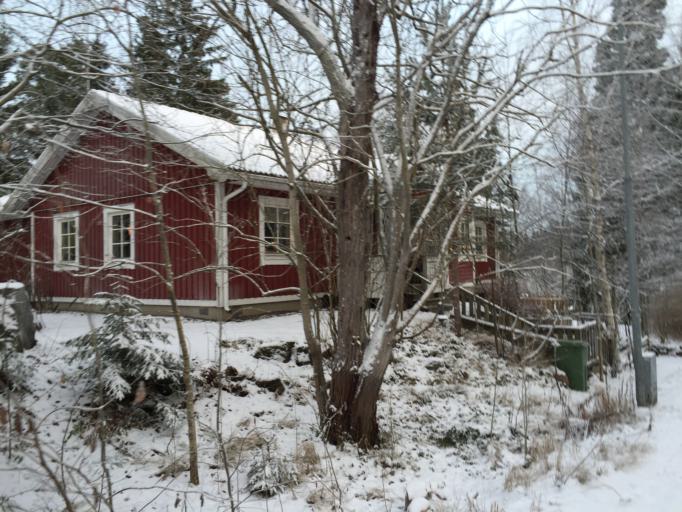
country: SE
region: Stockholm
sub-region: Salems Kommun
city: Ronninge
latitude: 59.1903
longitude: 17.7575
